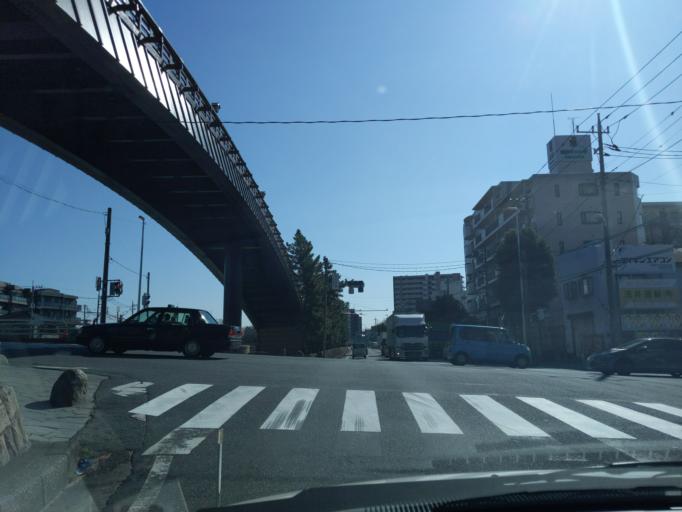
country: JP
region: Saitama
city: Soka
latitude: 35.8379
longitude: 139.8061
